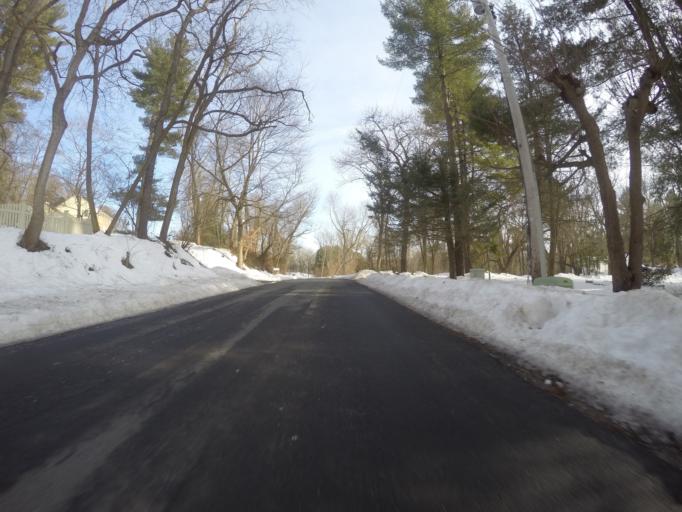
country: US
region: Maryland
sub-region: Baltimore County
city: Hunt Valley
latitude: 39.5717
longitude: -76.6323
